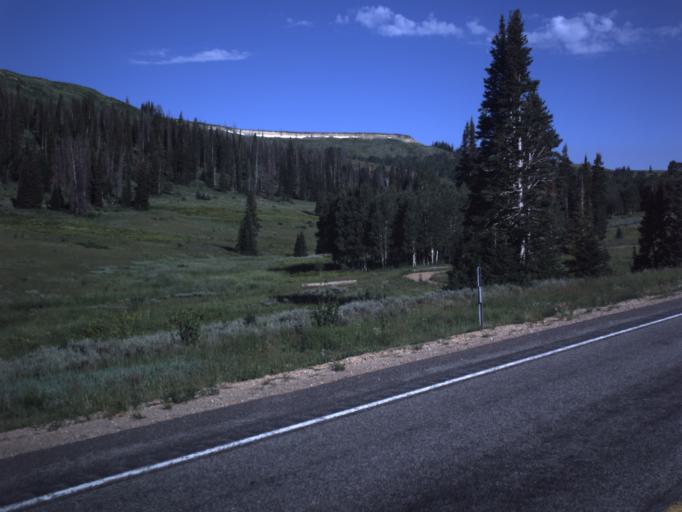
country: US
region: Utah
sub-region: Sanpete County
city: Fairview
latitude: 39.6021
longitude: -111.2736
